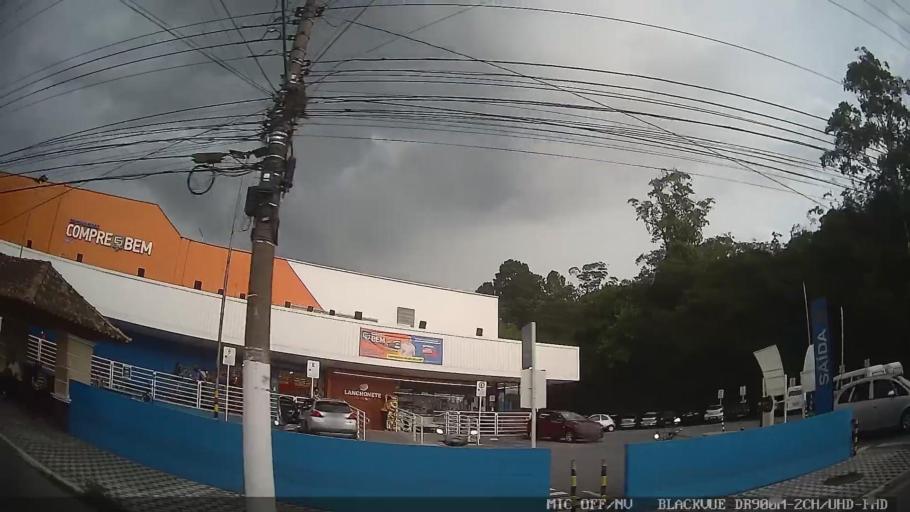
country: BR
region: Sao Paulo
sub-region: Ribeirao Pires
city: Ribeirao Pires
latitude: -23.7126
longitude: -46.4123
